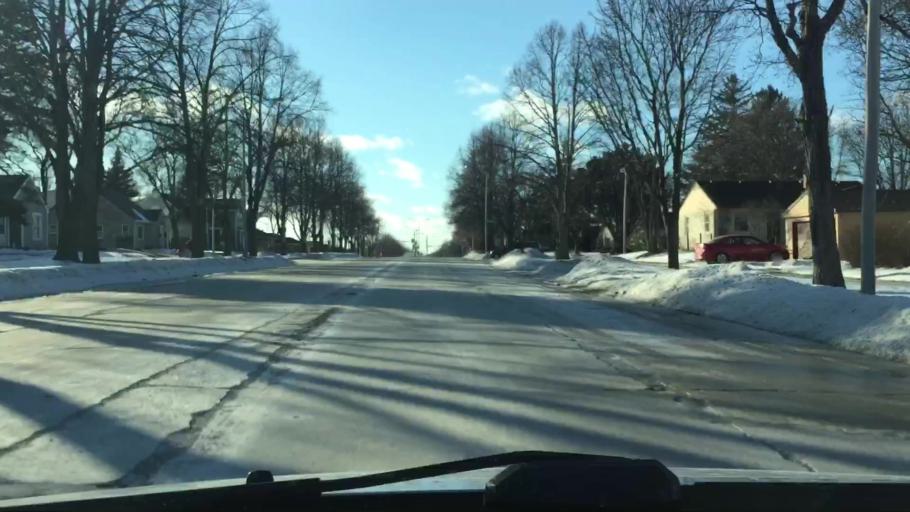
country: US
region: Wisconsin
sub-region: Milwaukee County
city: Greenfield
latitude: 42.9739
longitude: -87.9846
